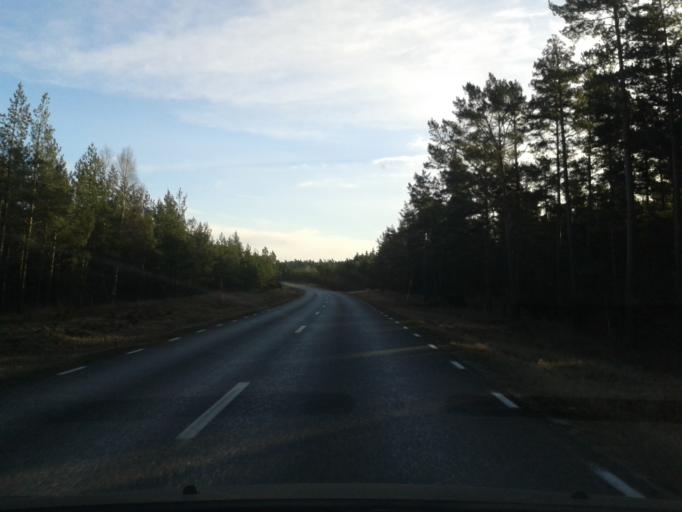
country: SE
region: Gotland
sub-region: Gotland
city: Hemse
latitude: 57.3907
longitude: 18.6480
